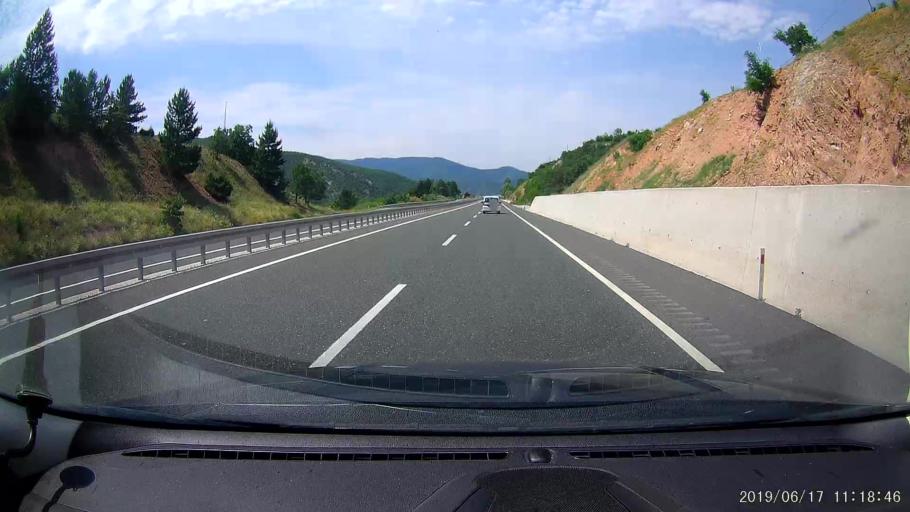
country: TR
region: Cankiri
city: Yaprakli
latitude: 40.9300
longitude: 33.8434
